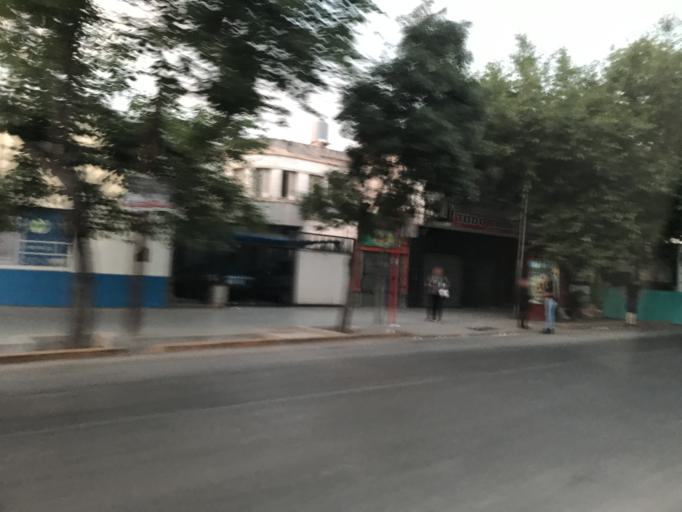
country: AR
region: Mendoza
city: Mendoza
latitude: -32.8928
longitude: -68.8330
